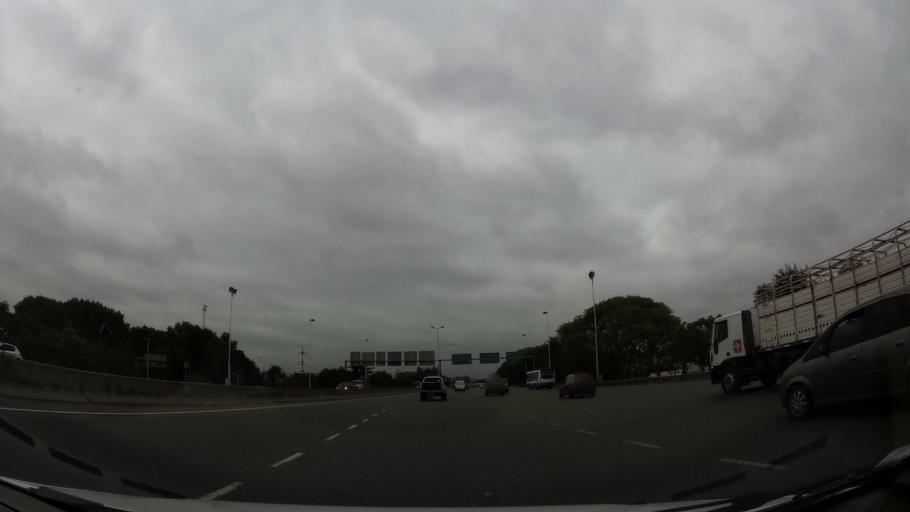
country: AR
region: Buenos Aires F.D.
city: Villa Lugano
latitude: -34.7021
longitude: -58.4981
